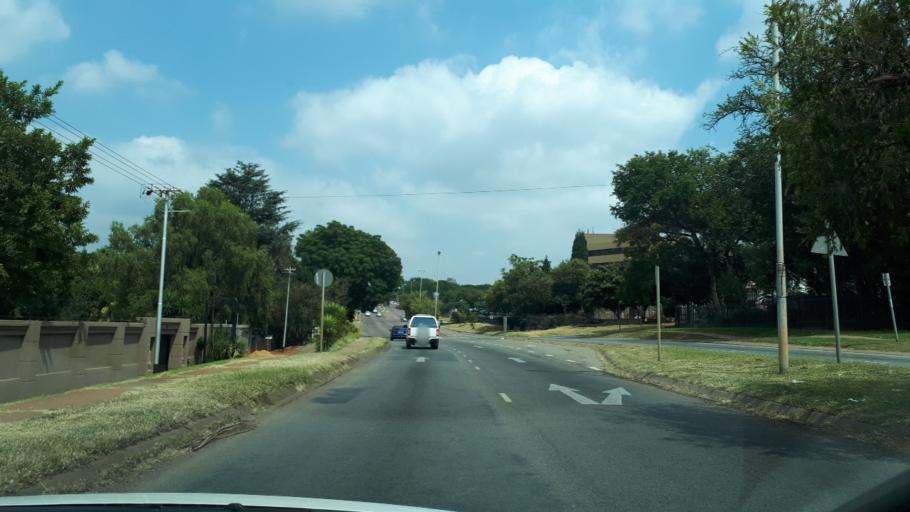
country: ZA
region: Gauteng
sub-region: City of Tshwane Metropolitan Municipality
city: Pretoria
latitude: -25.7436
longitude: 28.2981
